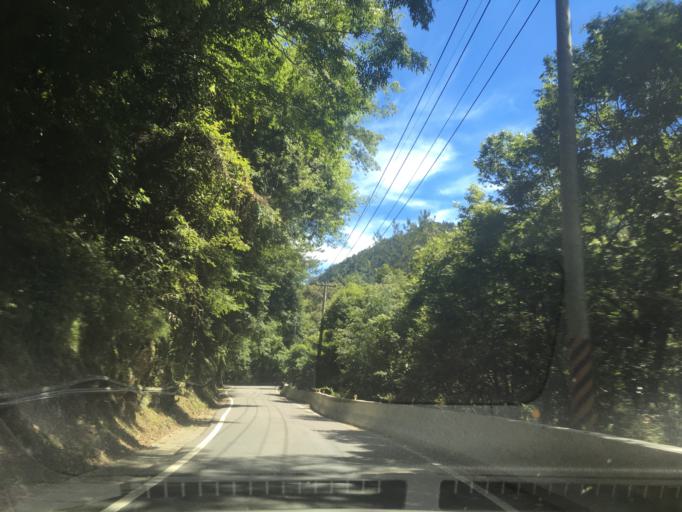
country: TW
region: Taiwan
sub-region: Nantou
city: Puli
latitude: 24.2155
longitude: 121.2655
